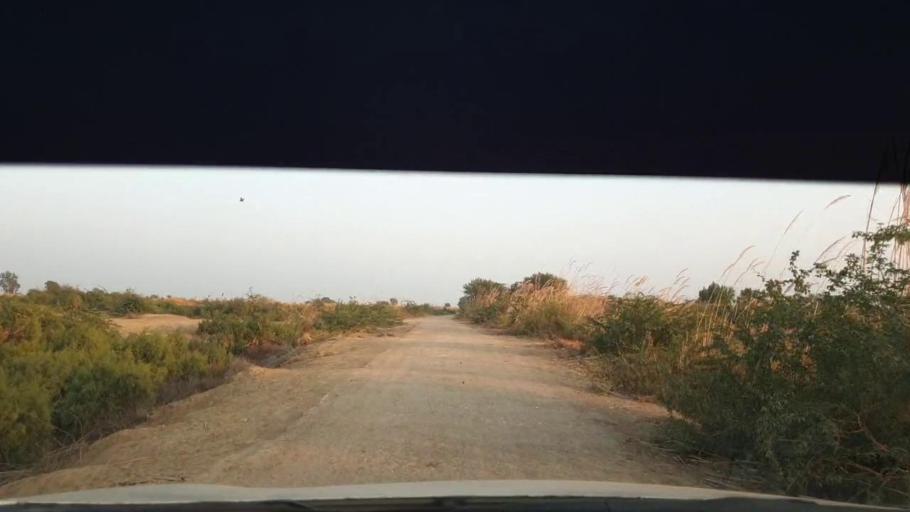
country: PK
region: Sindh
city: Berani
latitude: 25.7553
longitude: 69.0011
